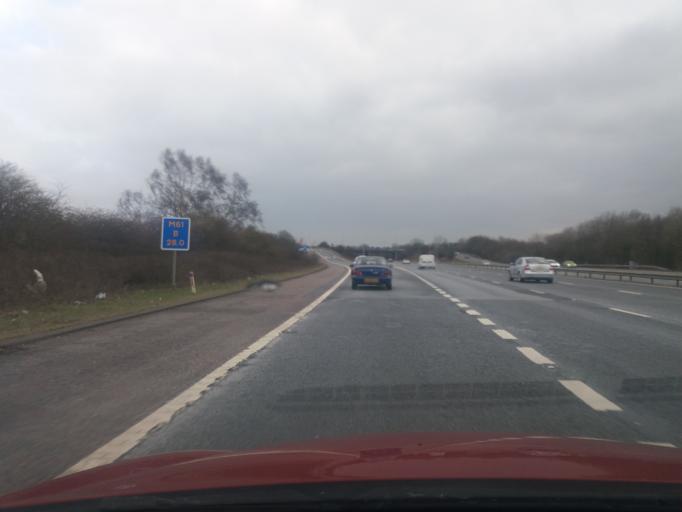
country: GB
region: England
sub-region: Lancashire
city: Chorley
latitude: 53.6741
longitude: -2.6269
